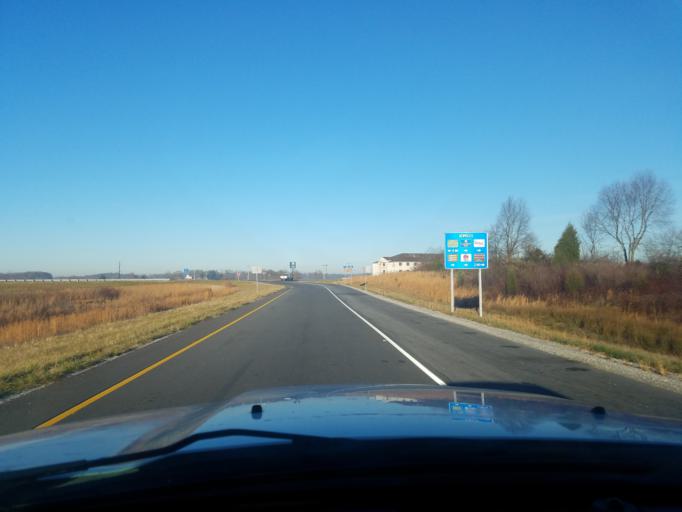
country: US
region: Indiana
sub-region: Dubois County
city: Ferdinand
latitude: 38.2065
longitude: -86.8641
